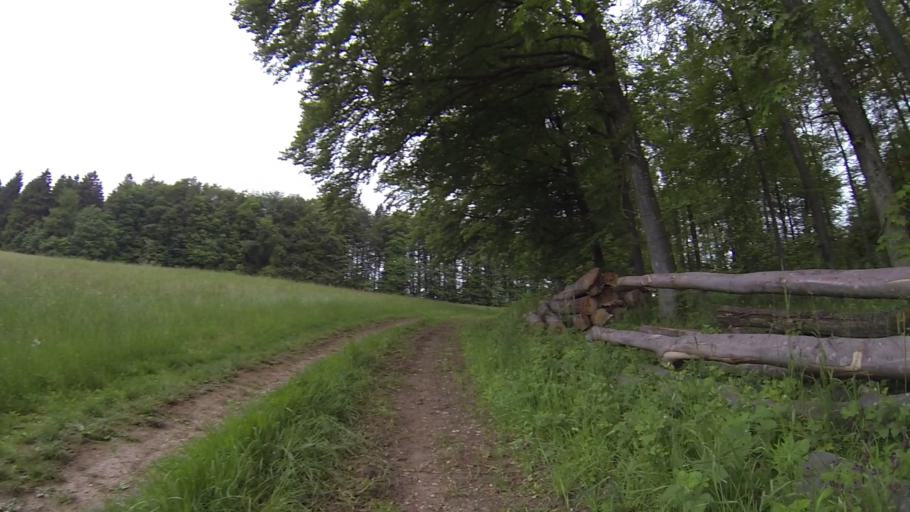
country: DE
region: Baden-Wuerttemberg
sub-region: Regierungsbezirk Stuttgart
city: Bartholoma
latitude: 48.7751
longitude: 9.9649
